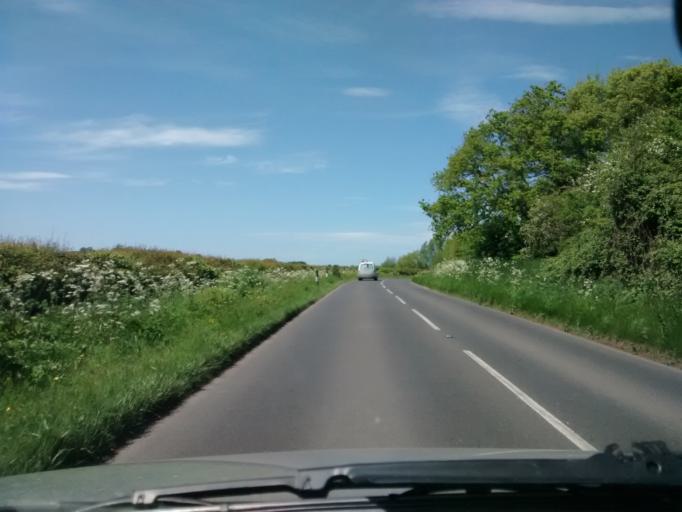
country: GB
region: England
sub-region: Bath and North East Somerset
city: Chew Magna
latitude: 51.3483
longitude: -2.6097
